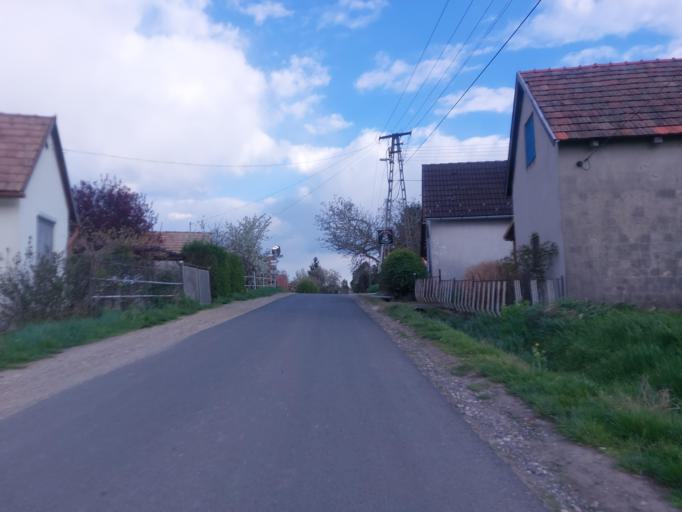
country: HU
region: Veszprem
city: Devecser
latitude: 47.1563
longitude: 17.3778
